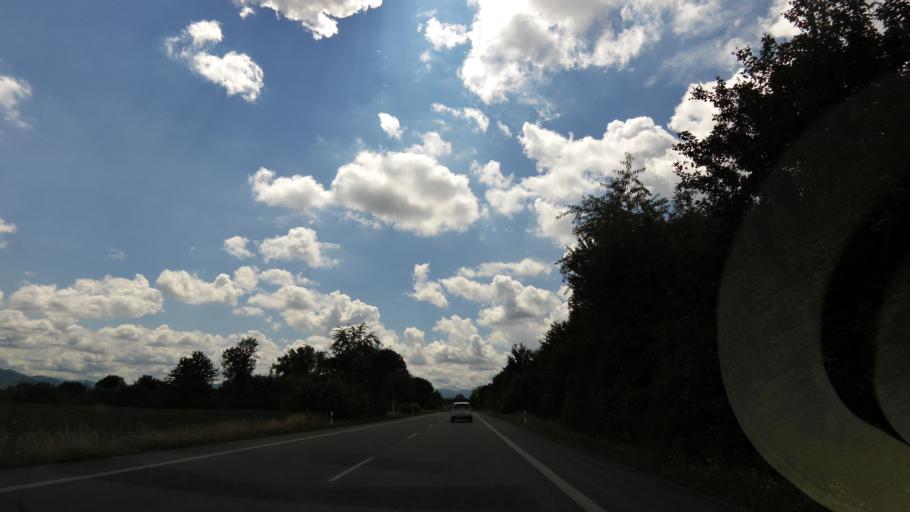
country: DE
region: Baden-Wuerttemberg
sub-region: Karlsruhe Region
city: Iffezheim
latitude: 48.8240
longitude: 8.1274
